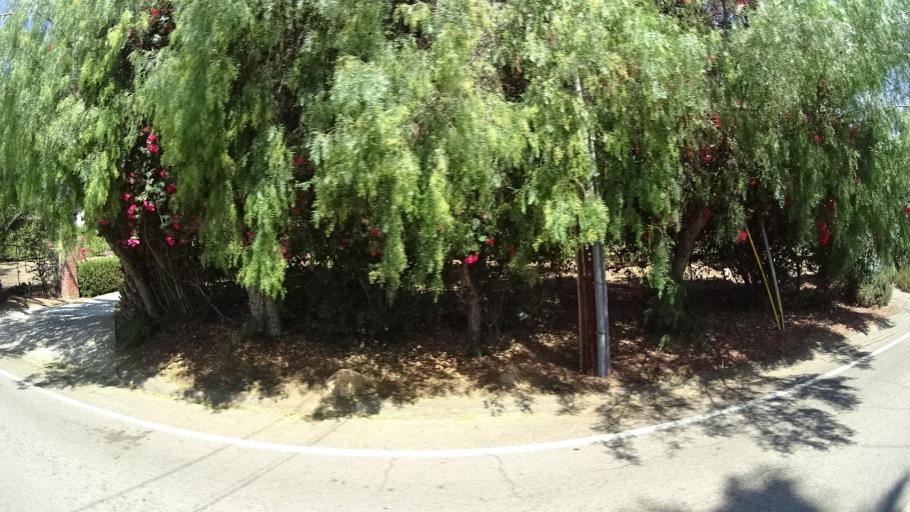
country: US
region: California
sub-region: San Diego County
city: Fallbrook
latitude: 33.3820
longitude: -117.2250
